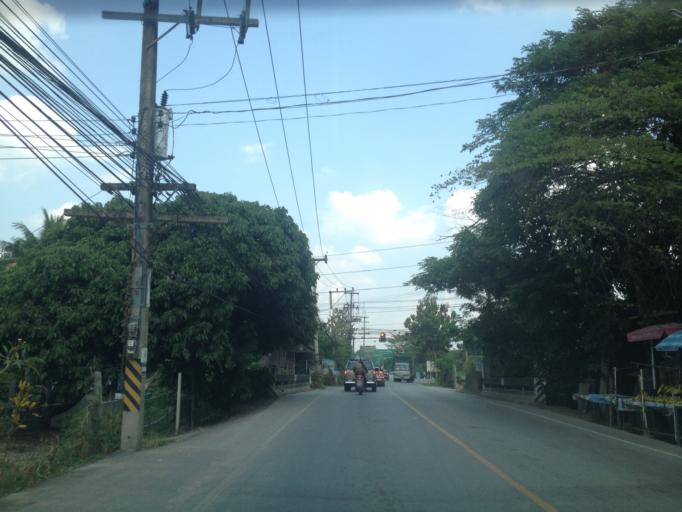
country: TH
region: Chiang Mai
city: Saraphi
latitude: 18.7182
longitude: 99.0416
